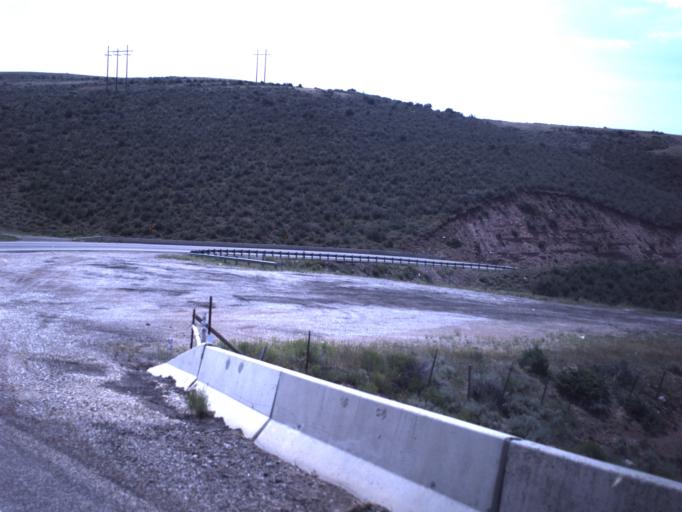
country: US
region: Utah
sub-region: Uintah County
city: Vernal
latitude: 40.6638
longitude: -109.4795
